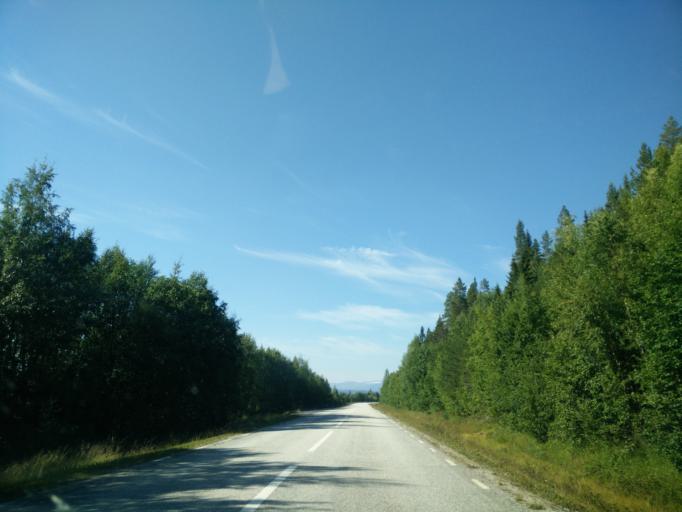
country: SE
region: Jaemtland
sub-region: Are Kommun
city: Jarpen
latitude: 62.8028
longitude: 13.5528
